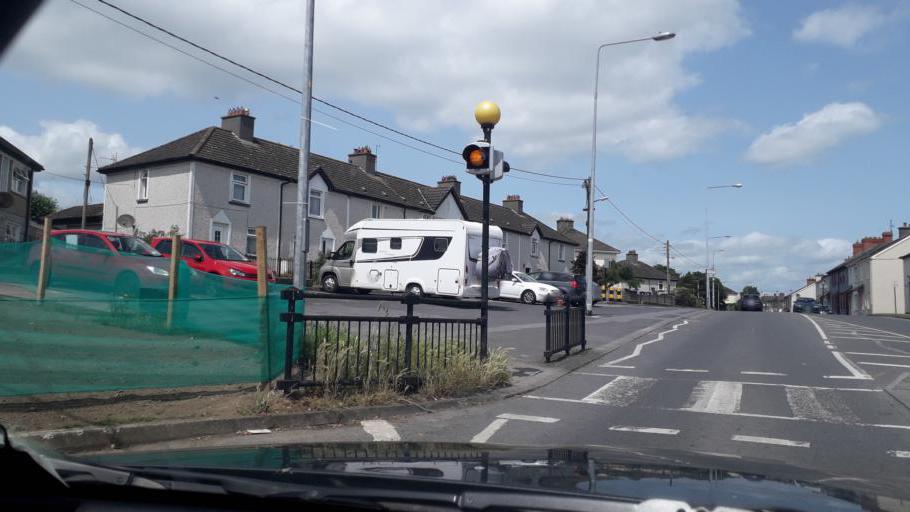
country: IE
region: Leinster
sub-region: Kilkenny
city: Kilkenny
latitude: 52.6554
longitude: -7.2605
